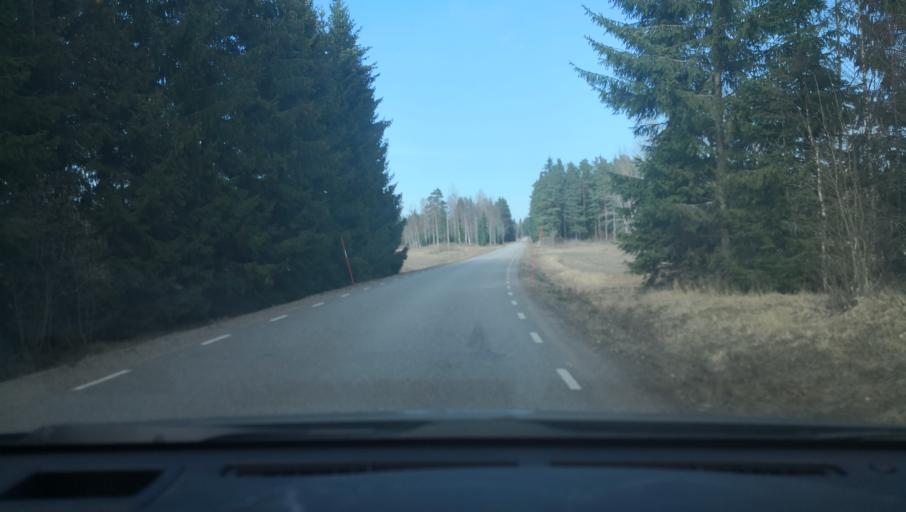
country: SE
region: Uppsala
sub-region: Heby Kommun
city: Heby
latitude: 59.9100
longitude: 16.8245
